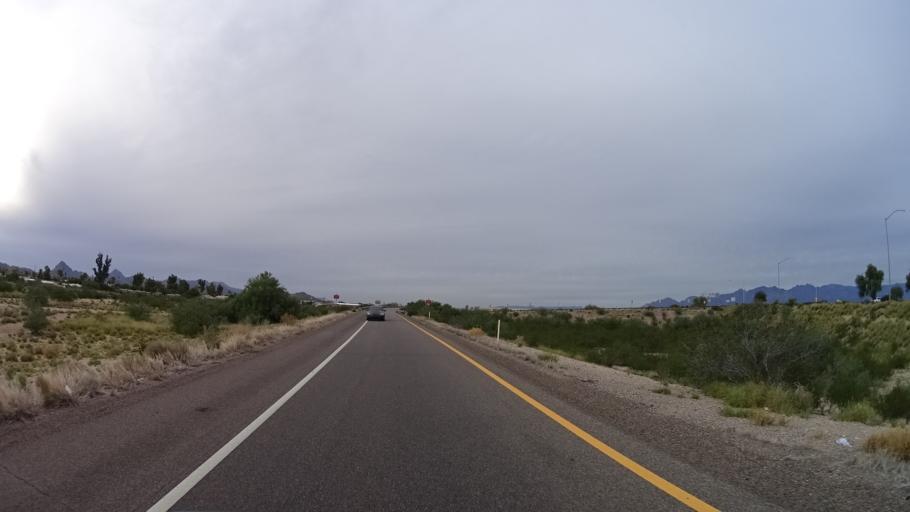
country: US
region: Arizona
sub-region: Pima County
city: South Tucson
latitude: 32.1751
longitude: -110.9451
